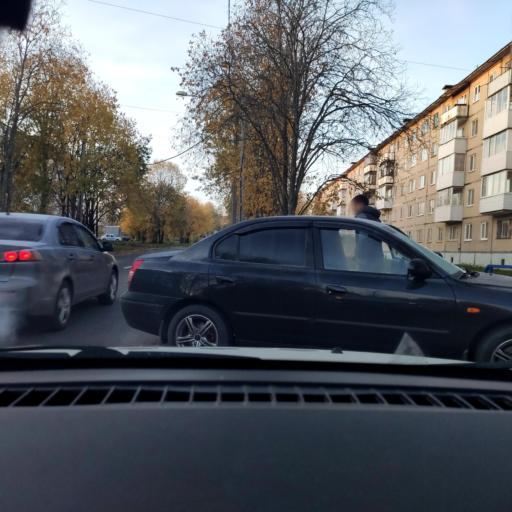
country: RU
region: Perm
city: Novyye Lyady
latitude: 58.0518
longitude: 56.5782
